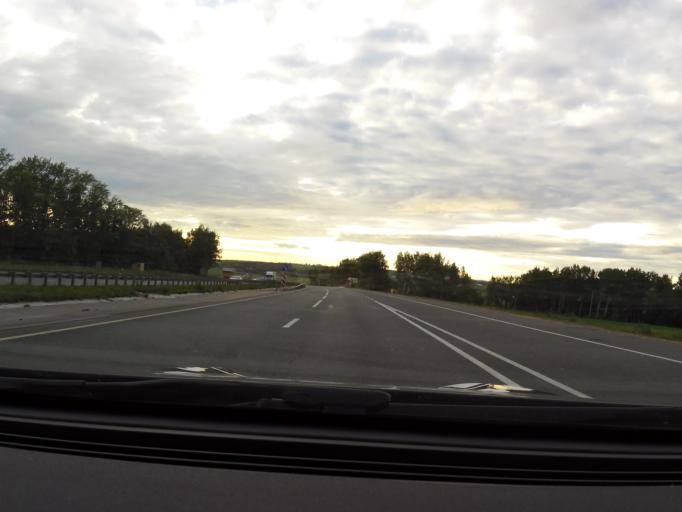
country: RU
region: Chuvashia
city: Kugesi
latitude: 55.9741
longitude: 47.3654
